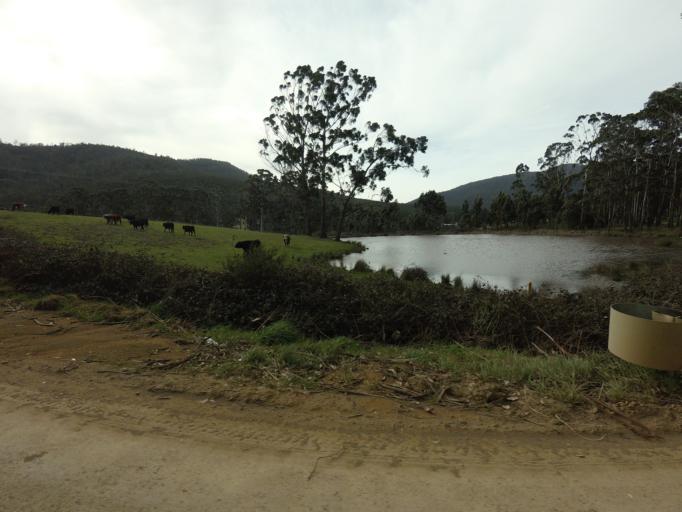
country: AU
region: Tasmania
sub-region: Huon Valley
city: Huonville
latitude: -43.0758
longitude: 147.0584
